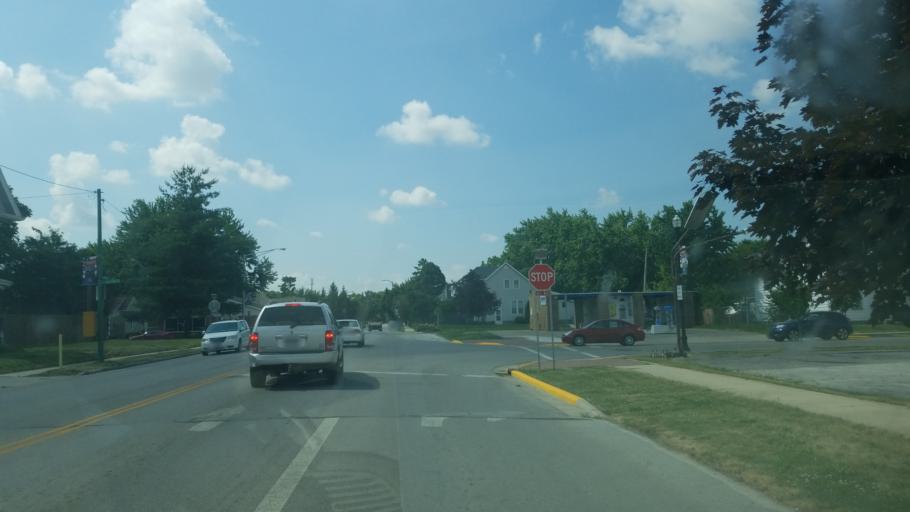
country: US
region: Ohio
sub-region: Auglaize County
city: Wapakoneta
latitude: 40.5706
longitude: -84.1838
